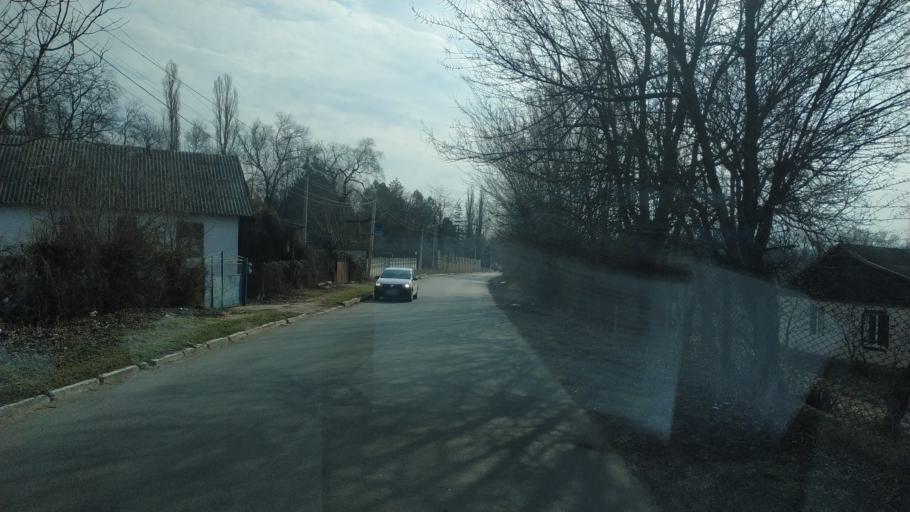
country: MD
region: Chisinau
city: Singera
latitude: 46.9262
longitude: 29.0499
